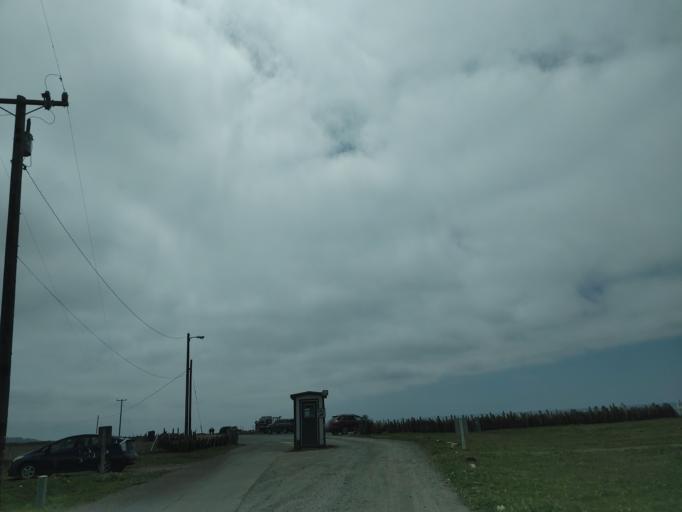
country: US
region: California
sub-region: Sonoma County
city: Sea Ranch
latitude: 38.9515
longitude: -123.7374
